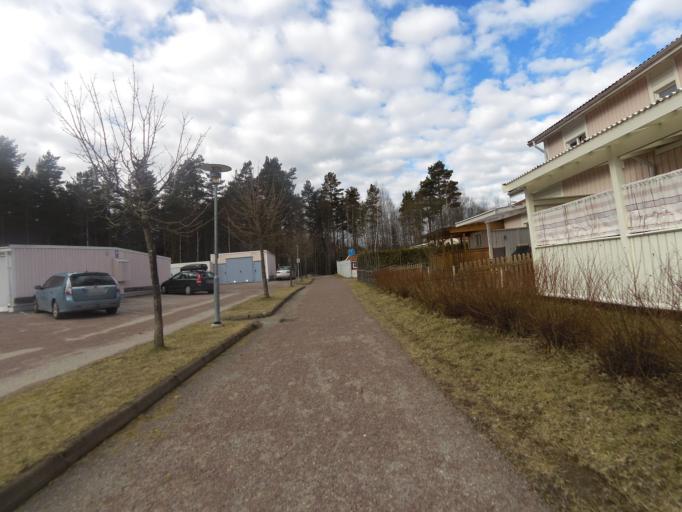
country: SE
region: Gaevleborg
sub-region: Gavle Kommun
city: Gavle
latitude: 60.6968
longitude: 17.0888
